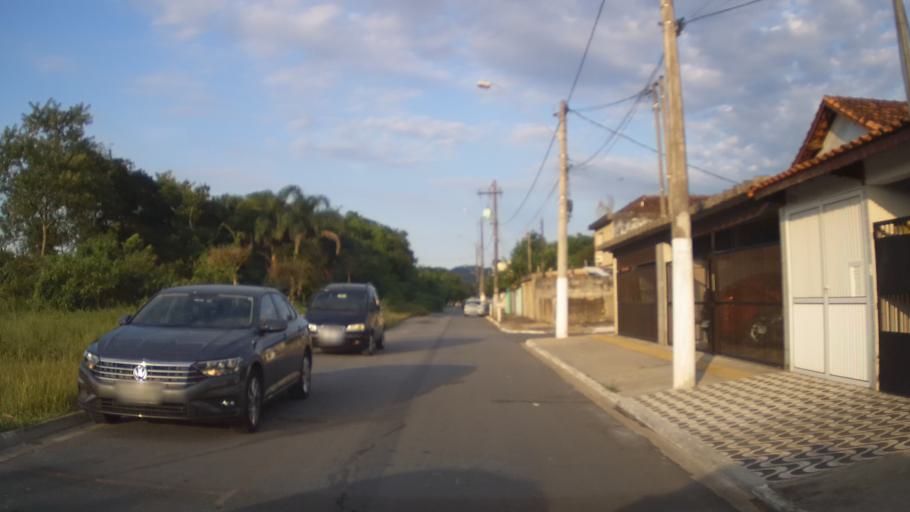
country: BR
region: Sao Paulo
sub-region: Praia Grande
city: Praia Grande
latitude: -23.9941
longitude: -46.4258
